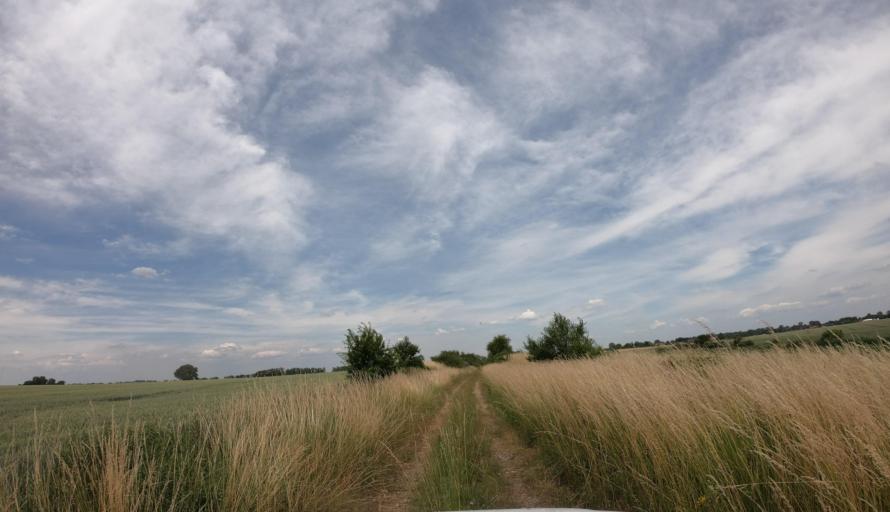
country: PL
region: West Pomeranian Voivodeship
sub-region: Powiat pyrzycki
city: Kozielice
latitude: 53.1313
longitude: 14.8513
